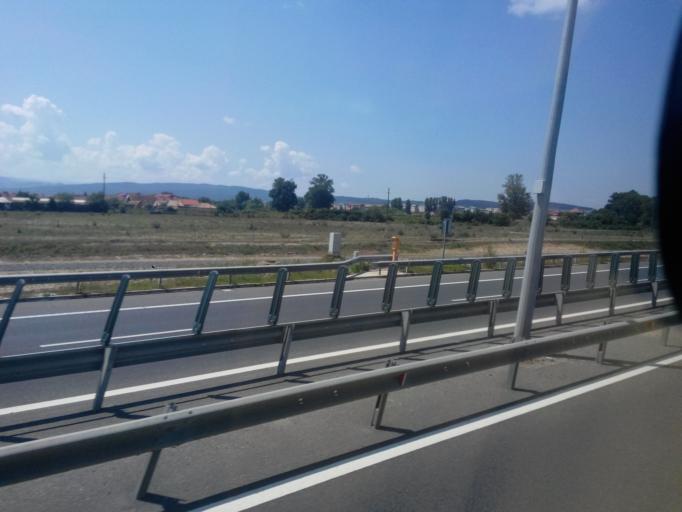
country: RO
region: Alba
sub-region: Municipiul Sebes
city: Sebes
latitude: 45.9726
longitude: 23.5690
